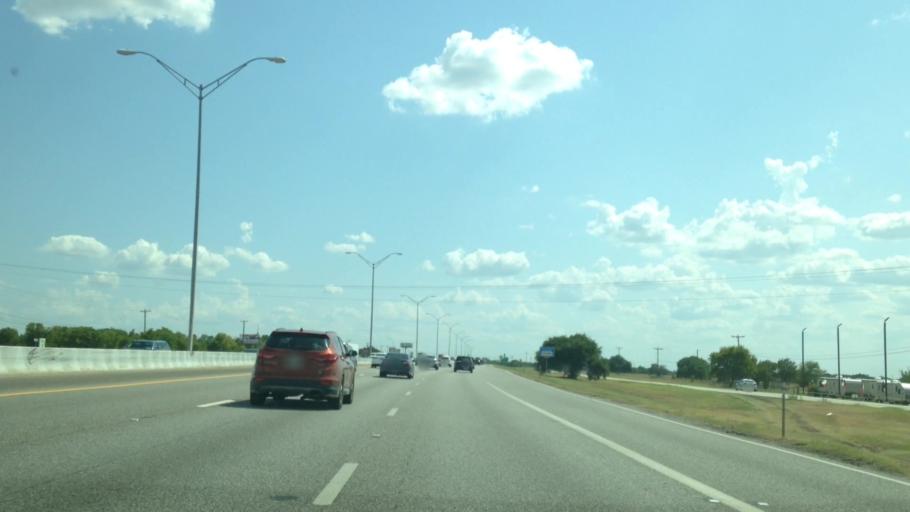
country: US
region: Texas
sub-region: Williamson County
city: Georgetown
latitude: 30.6038
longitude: -97.6862
